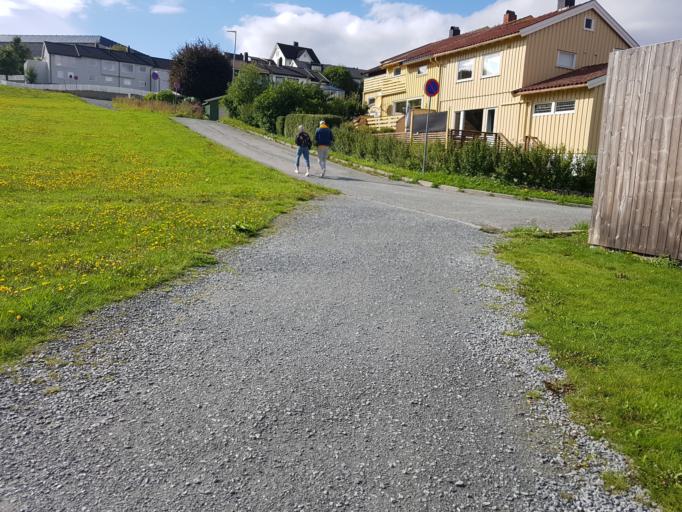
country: NO
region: Sor-Trondelag
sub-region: Trondheim
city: Trondheim
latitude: 63.4243
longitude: 10.4397
